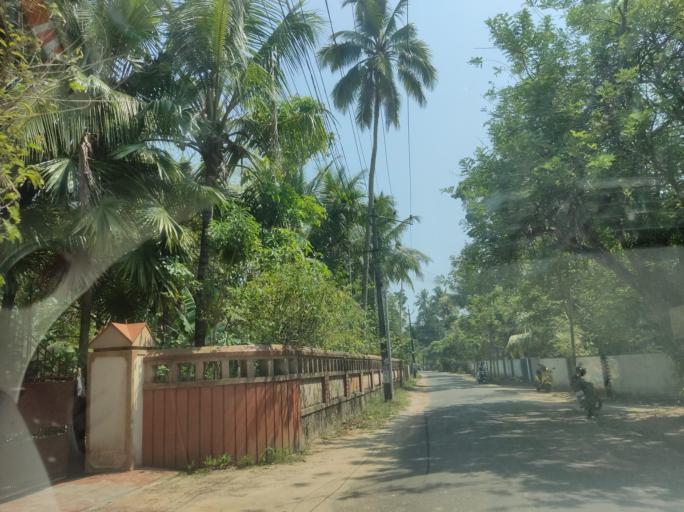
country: IN
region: Kerala
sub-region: Alappuzha
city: Vayalar
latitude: 9.7021
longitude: 76.3032
